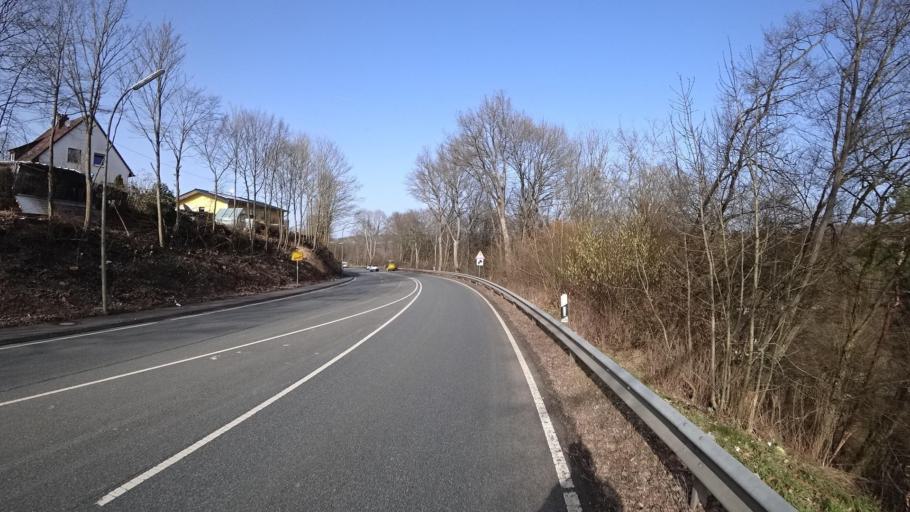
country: DE
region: Rheinland-Pfalz
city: Bruchertseifen
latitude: 50.7676
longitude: 7.7178
